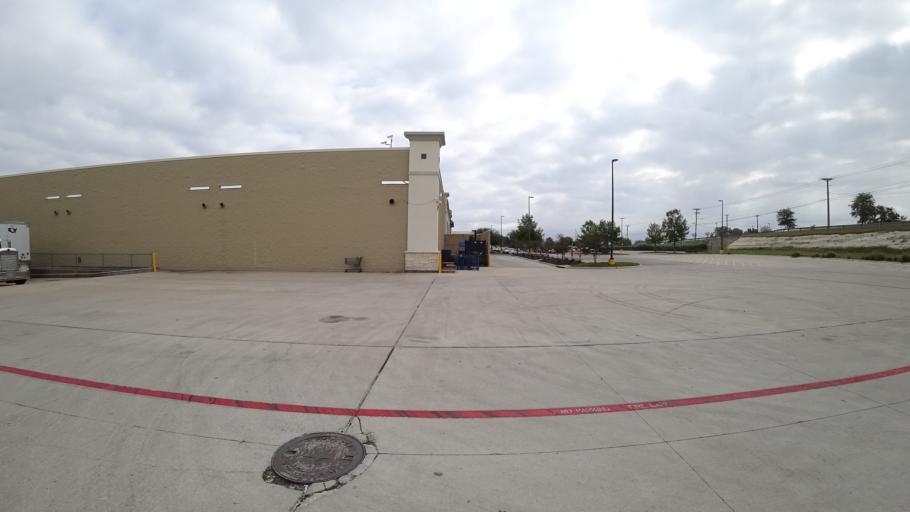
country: US
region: Texas
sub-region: Travis County
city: Pflugerville
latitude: 30.4532
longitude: -97.6080
